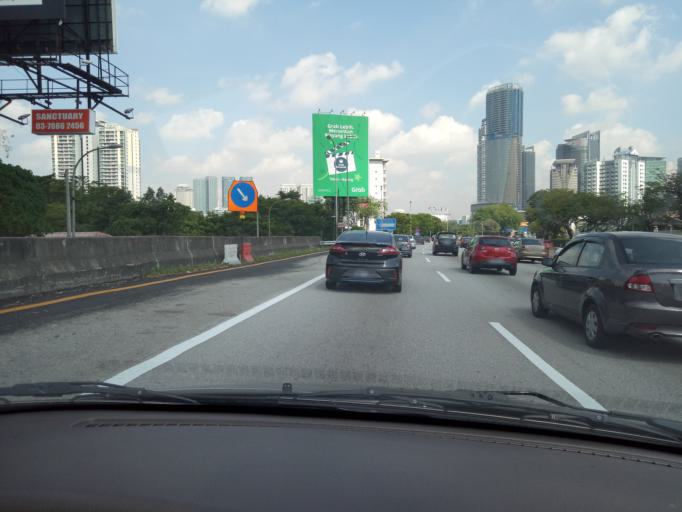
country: MY
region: Kuala Lumpur
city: Kuala Lumpur
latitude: 3.1122
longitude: 101.6839
